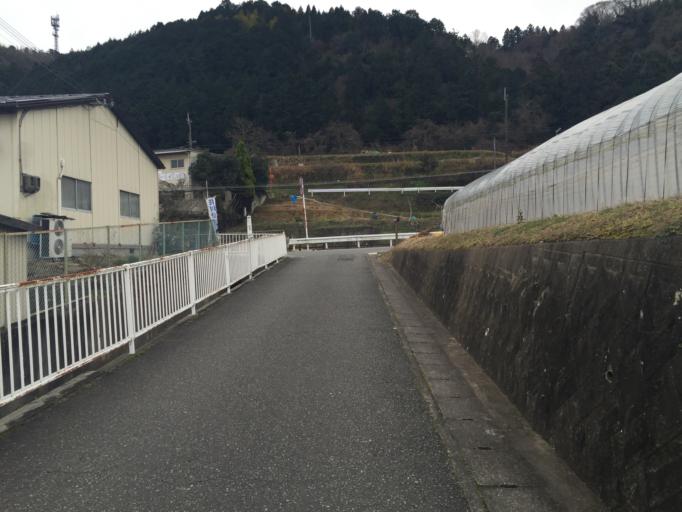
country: JP
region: Wakayama
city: Hashimoto
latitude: 34.3090
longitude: 135.6086
